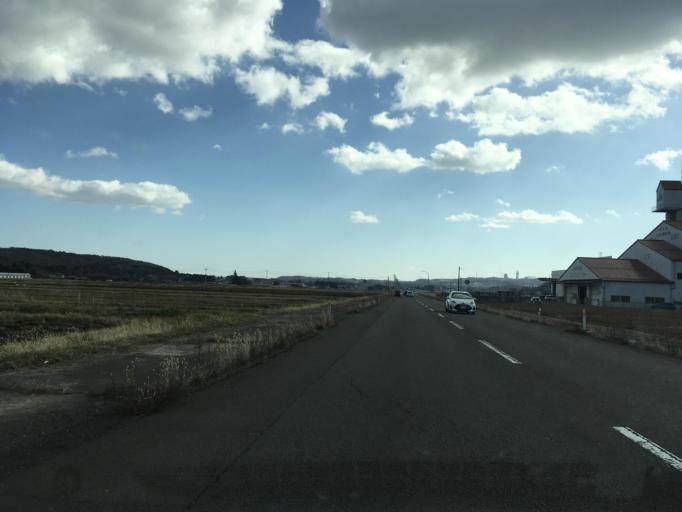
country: JP
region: Miyagi
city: Tomiya
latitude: 38.3484
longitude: 140.7836
